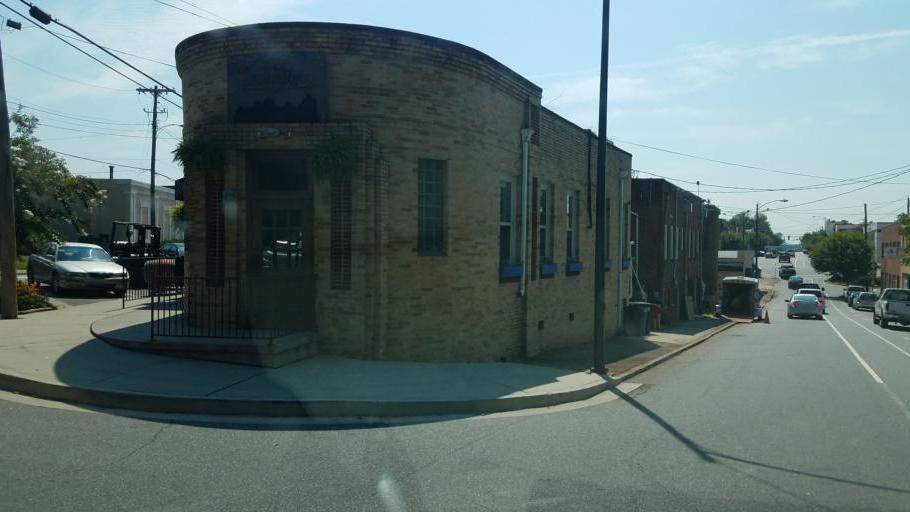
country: US
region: North Carolina
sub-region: Burke County
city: Morganton
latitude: 35.7477
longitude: -81.6912
